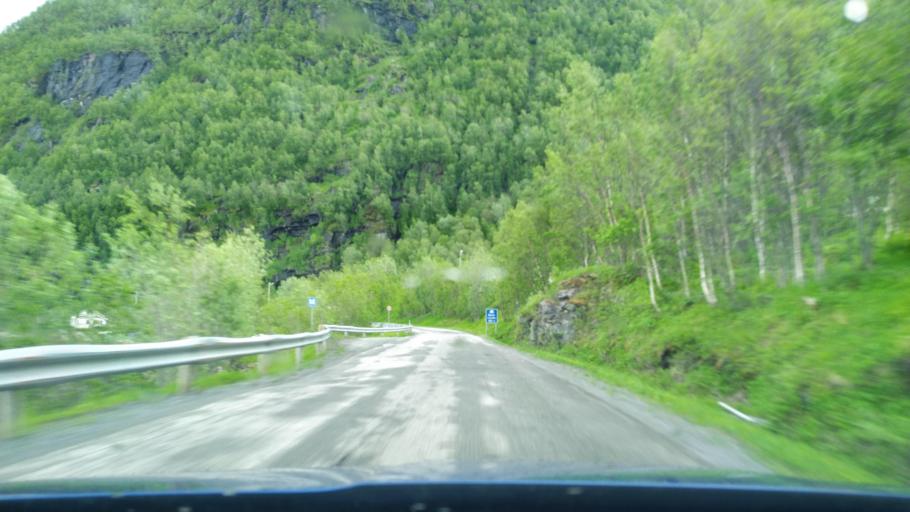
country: NO
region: Troms
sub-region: Lenvik
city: Finnsnes
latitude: 69.1459
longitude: 17.9405
